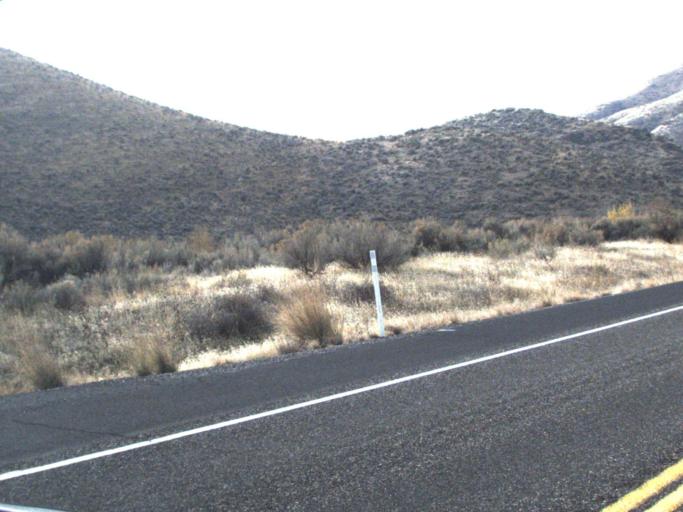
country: US
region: Washington
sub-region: Asotin County
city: Clarkston Heights-Vineland
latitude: 46.4036
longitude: -117.2472
